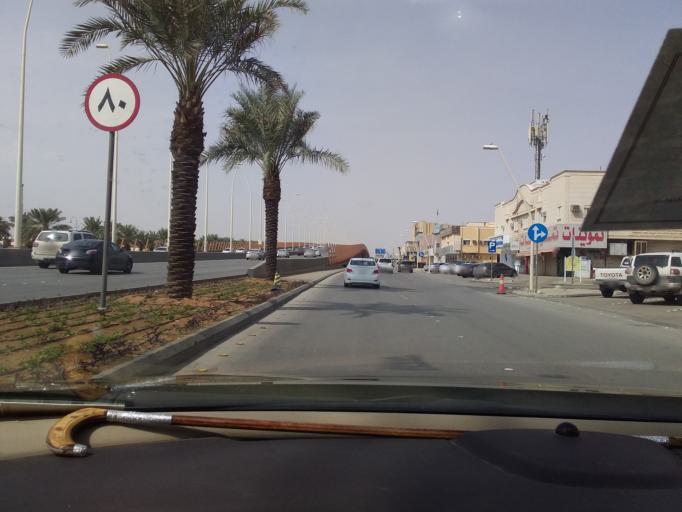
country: SA
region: Ar Riyad
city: Riyadh
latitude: 24.7401
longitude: 46.7054
